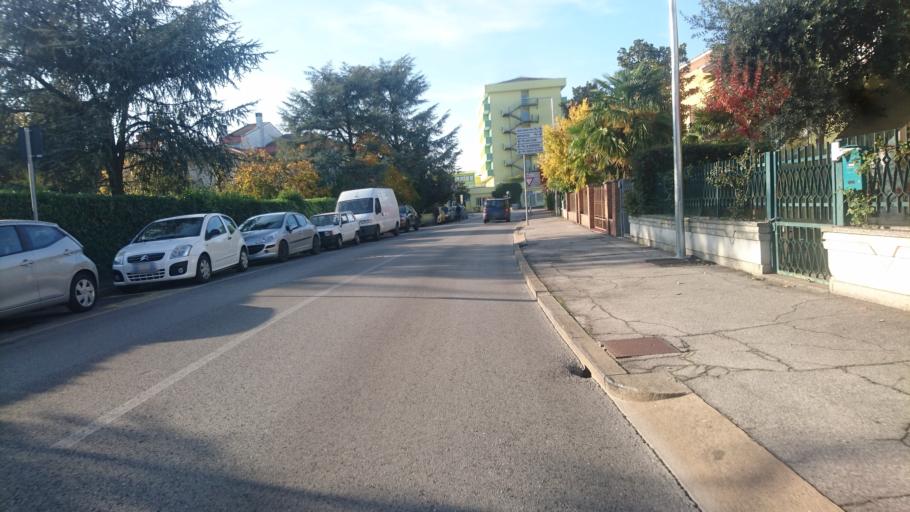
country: IT
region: Veneto
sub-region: Provincia di Padova
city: Abano Terme
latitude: 45.3476
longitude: 11.7900
